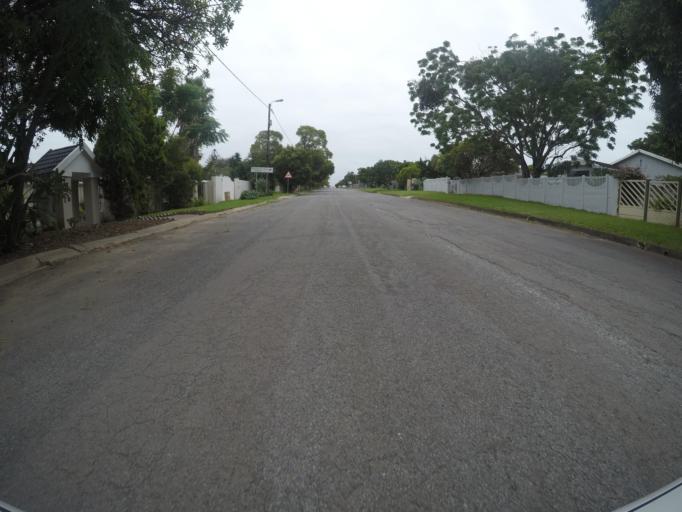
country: ZA
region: Eastern Cape
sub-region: Buffalo City Metropolitan Municipality
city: East London
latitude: -32.9722
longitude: 27.9355
